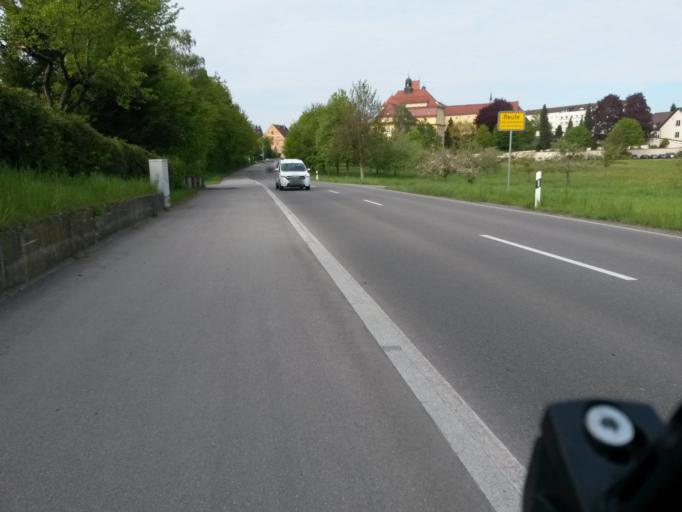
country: DE
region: Baden-Wuerttemberg
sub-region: Tuebingen Region
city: Bad Waldsee
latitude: 47.9031
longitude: 9.7072
